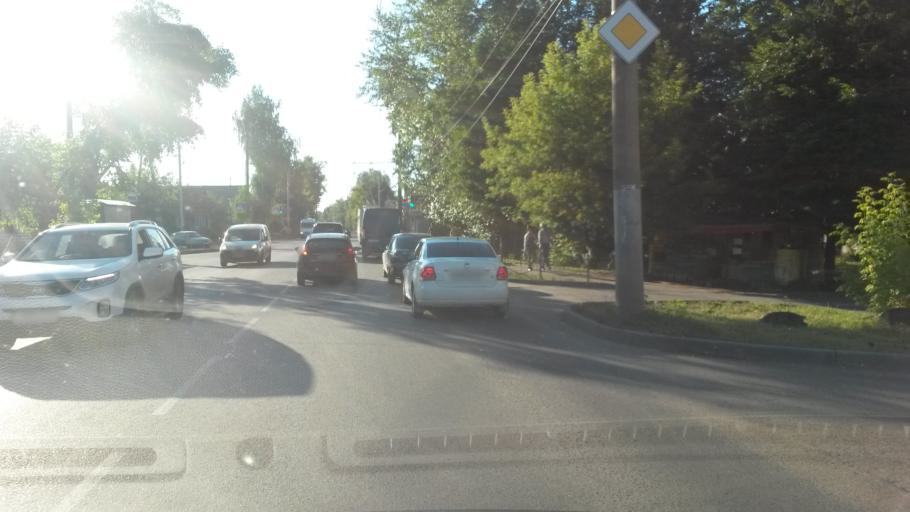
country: RU
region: Ivanovo
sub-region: Gorod Ivanovo
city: Ivanovo
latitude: 57.0113
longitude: 40.9385
